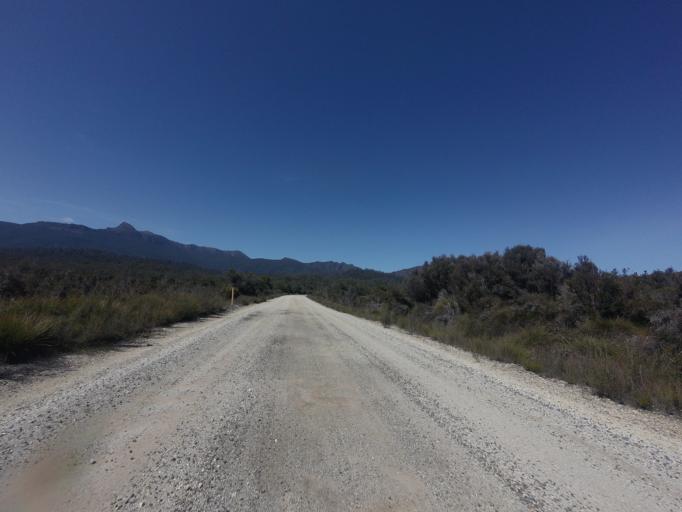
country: AU
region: Tasmania
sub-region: Huon Valley
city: Geeveston
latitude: -42.8974
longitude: 146.3742
